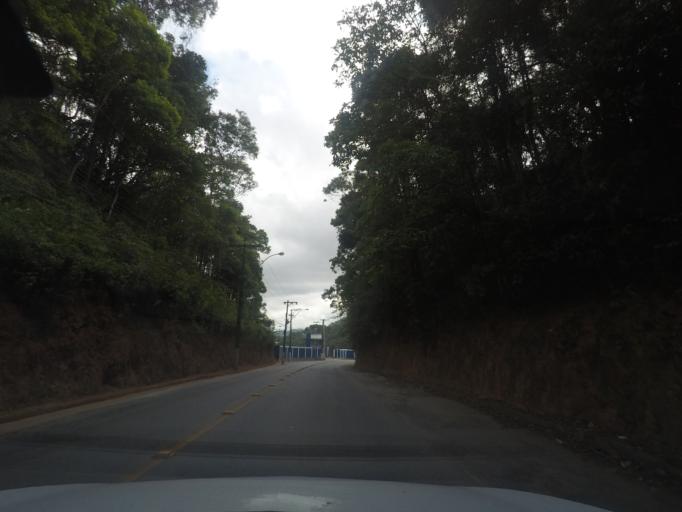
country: BR
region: Rio de Janeiro
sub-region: Teresopolis
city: Teresopolis
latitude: -22.3956
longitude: -42.9599
